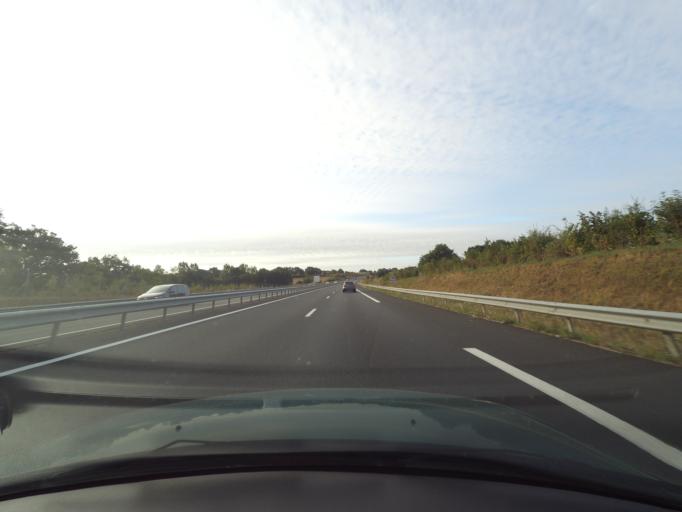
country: FR
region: Pays de la Loire
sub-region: Departement de Maine-et-Loire
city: La Tessoualle
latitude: 47.0172
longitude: -0.8755
